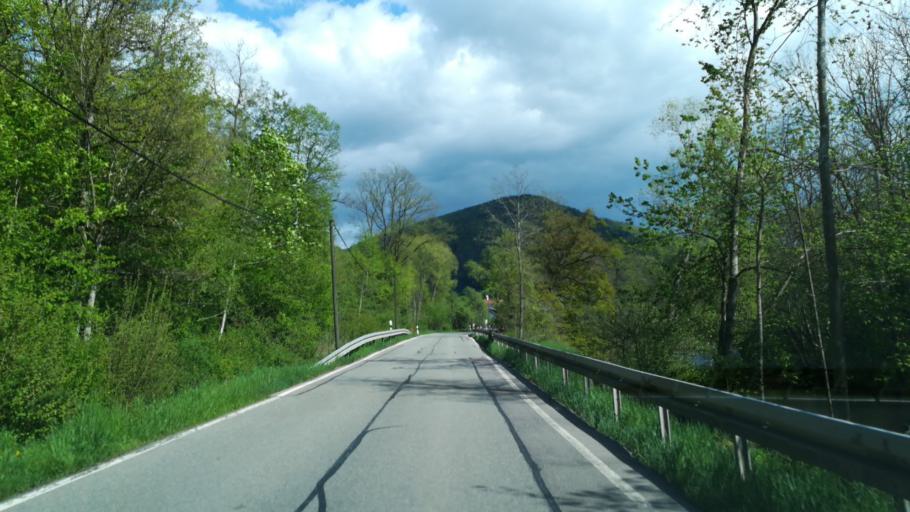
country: DE
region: Baden-Wuerttemberg
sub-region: Freiburg Region
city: Blumberg
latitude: 47.8391
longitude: 8.4949
